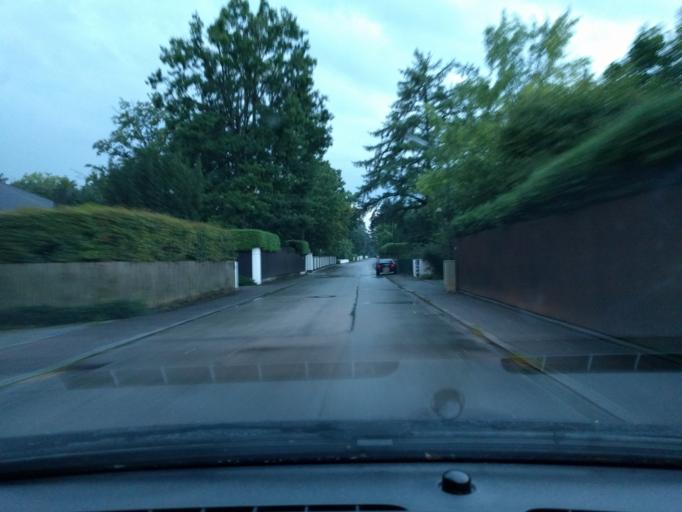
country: DE
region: Bavaria
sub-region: Upper Bavaria
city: Pullach im Isartal
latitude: 48.0518
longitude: 11.5387
